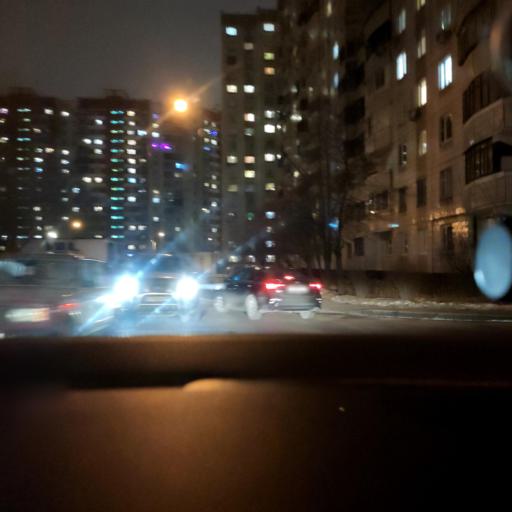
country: RU
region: Moskovskaya
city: Reutov
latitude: 55.7391
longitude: 37.8618
